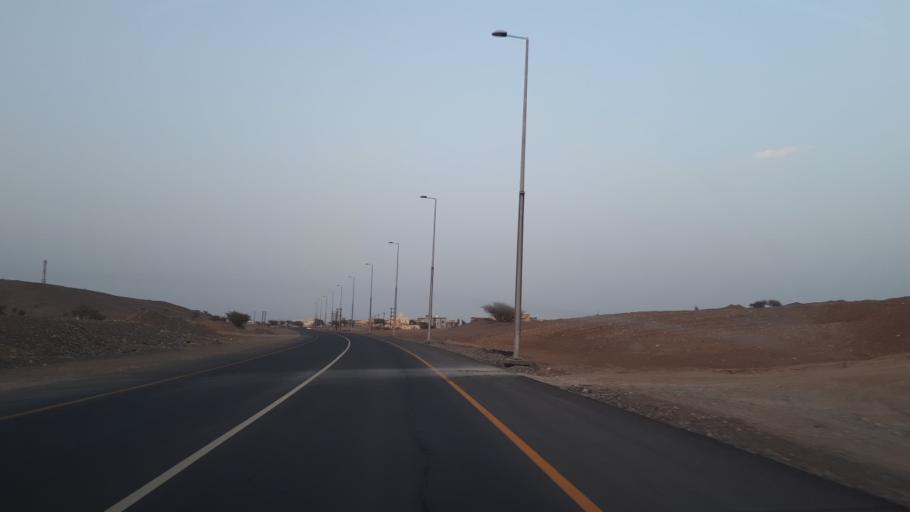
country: OM
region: Al Batinah
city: Rustaq
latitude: 23.5407
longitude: 57.5231
